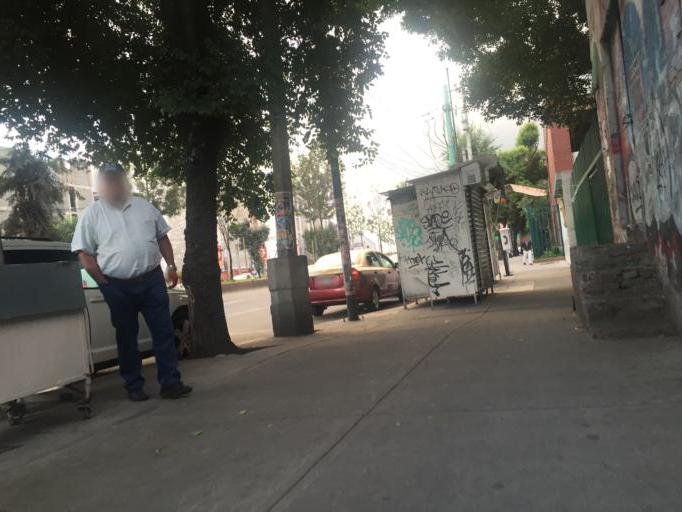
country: MX
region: Mexico City
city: Iztapalapa
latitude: 19.3554
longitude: -99.0850
